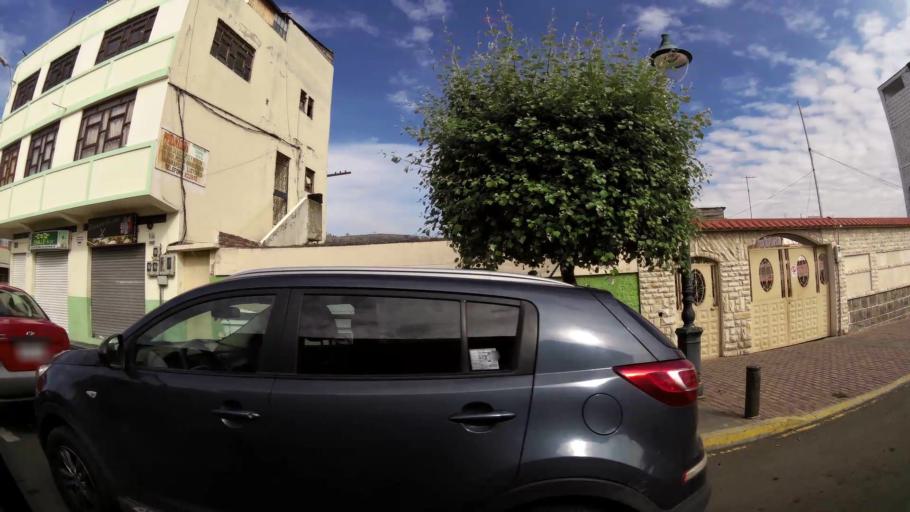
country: EC
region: Tungurahua
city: Ambato
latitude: -1.2442
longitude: -78.6318
